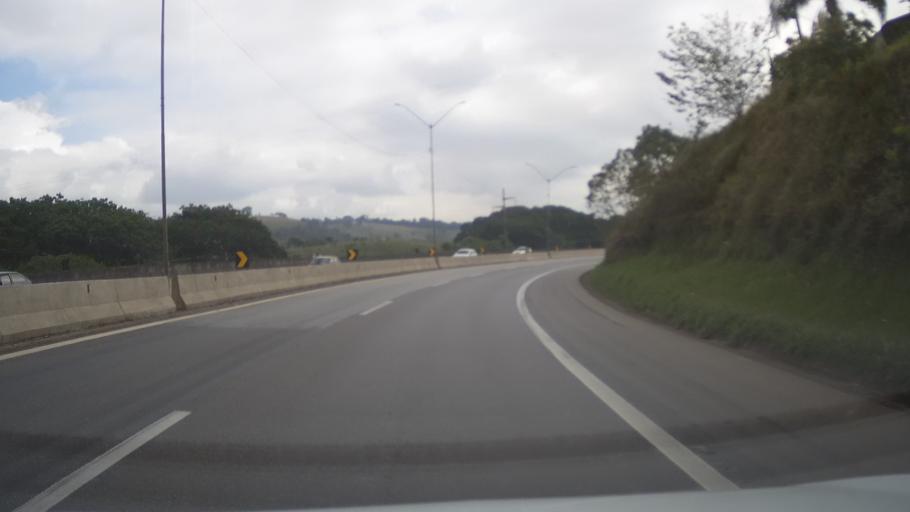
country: BR
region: Minas Gerais
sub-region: Extrema
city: Extrema
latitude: -22.8265
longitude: -46.3136
